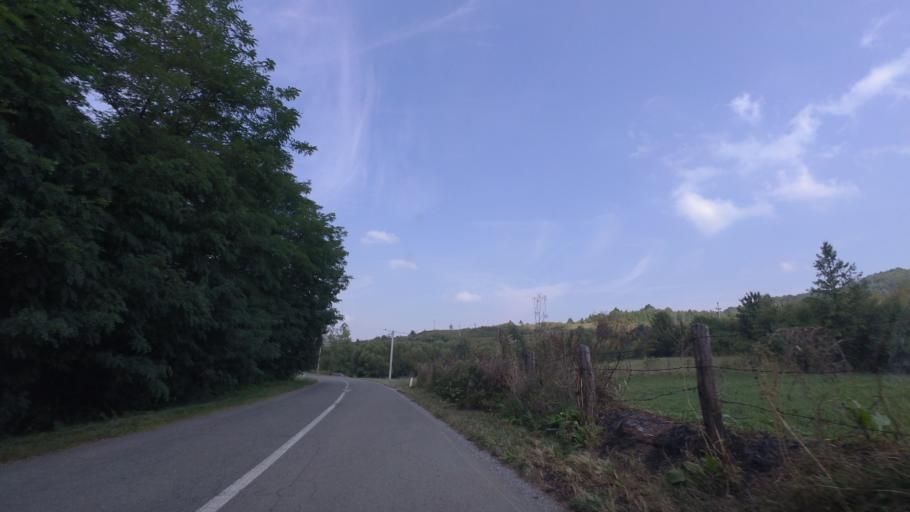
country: BA
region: Federation of Bosnia and Herzegovina
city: Zboriste
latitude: 45.1798
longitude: 16.1349
